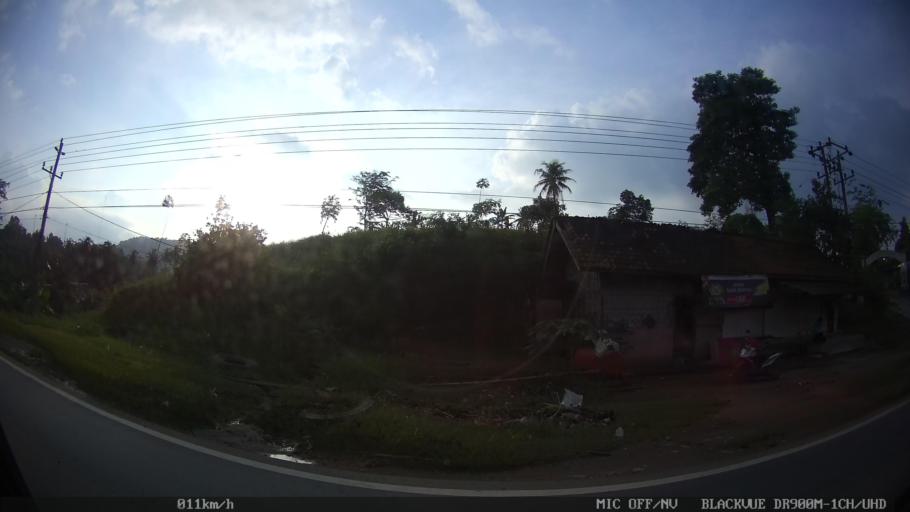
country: ID
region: Lampung
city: Panjang
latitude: -5.4040
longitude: 105.3503
